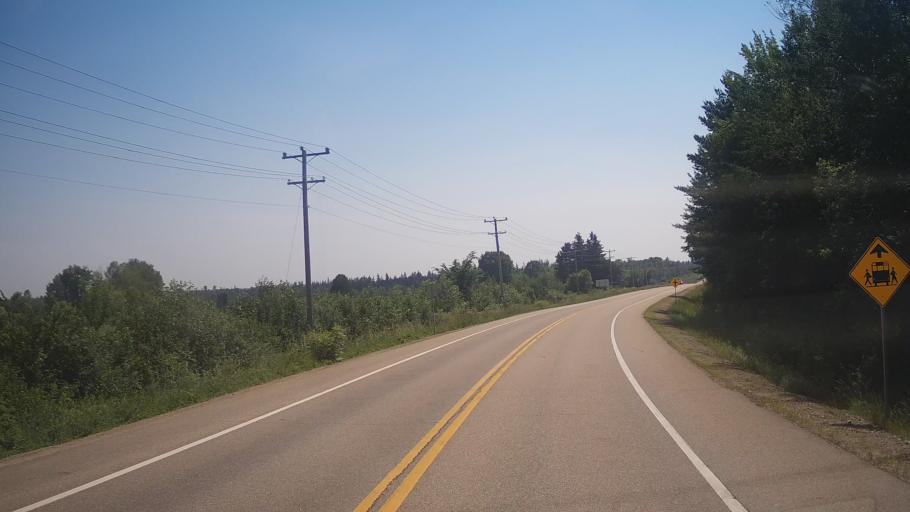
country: CA
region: Ontario
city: Pembroke
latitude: 45.8286
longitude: -77.0139
